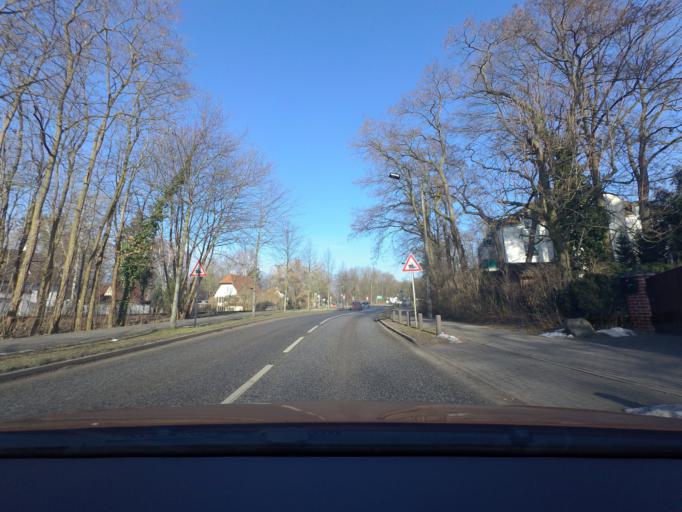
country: DE
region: Berlin
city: Blankenfelde
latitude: 52.6463
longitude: 13.3766
